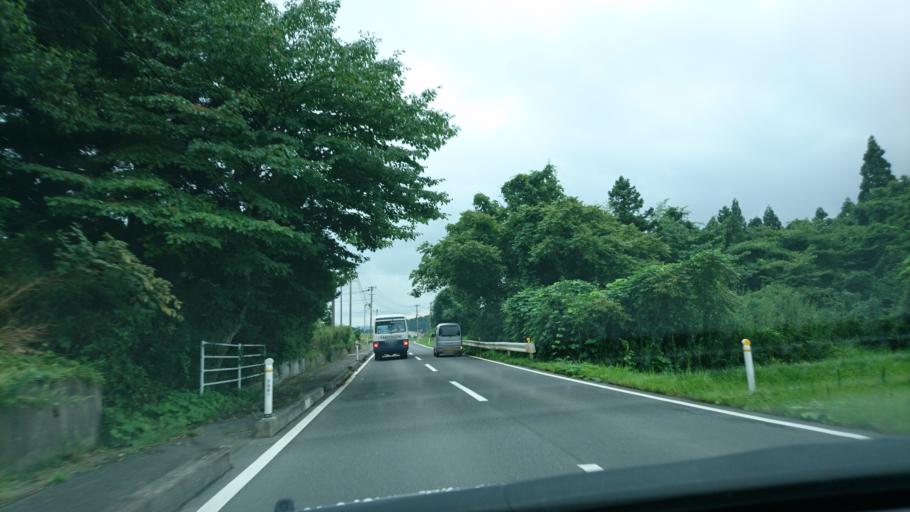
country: JP
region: Iwate
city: Ichinoseki
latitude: 38.8059
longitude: 140.9322
